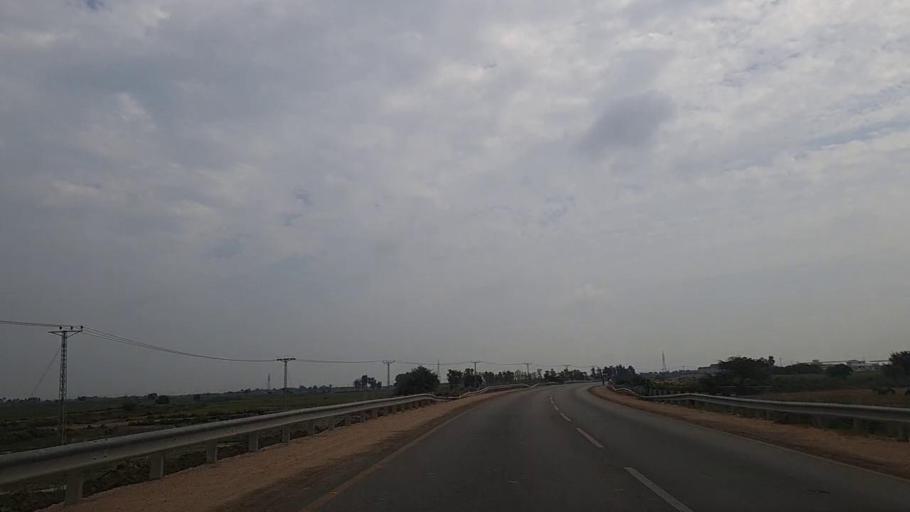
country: PK
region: Sindh
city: Daro Mehar
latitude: 24.6181
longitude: 68.0838
